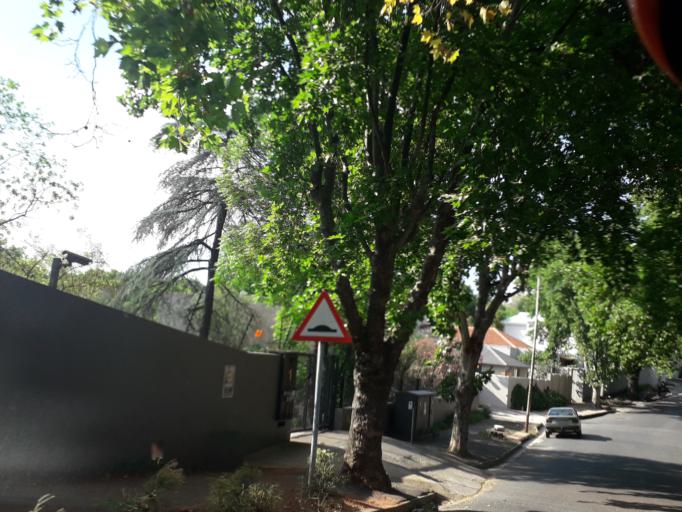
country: ZA
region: Gauteng
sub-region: City of Johannesburg Metropolitan Municipality
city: Johannesburg
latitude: -26.1494
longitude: 28.0327
